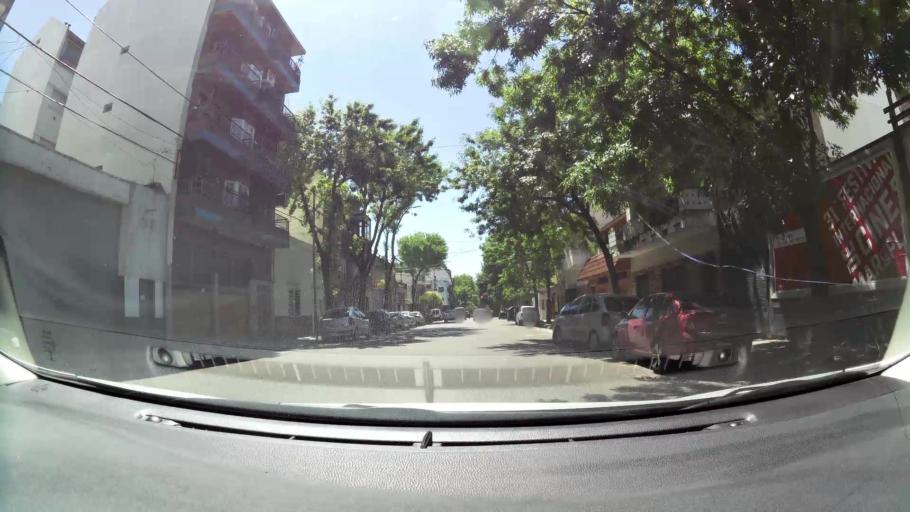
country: AR
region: Buenos Aires F.D.
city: Buenos Aires
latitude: -34.6282
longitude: -58.4079
